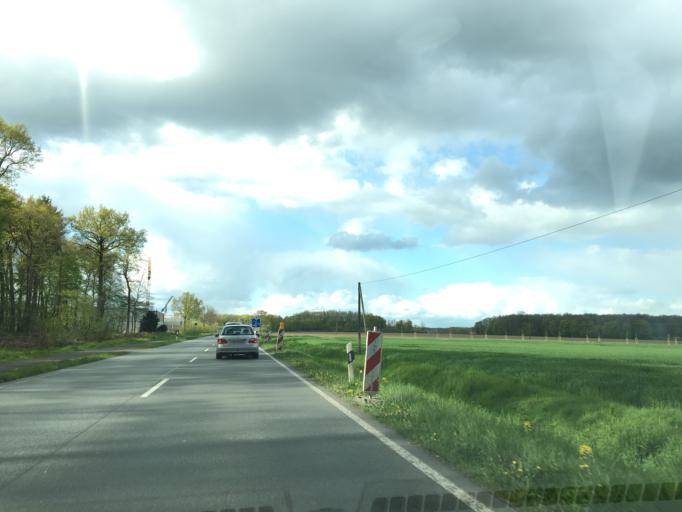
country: DE
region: North Rhine-Westphalia
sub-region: Regierungsbezirk Munster
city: Senden
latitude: 51.8943
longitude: 7.4935
